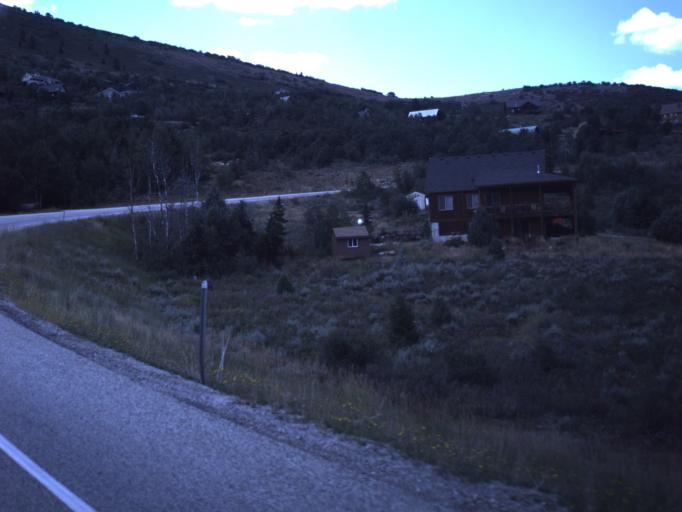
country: US
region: Idaho
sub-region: Bear Lake County
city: Paris
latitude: 41.9222
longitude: -111.4277
